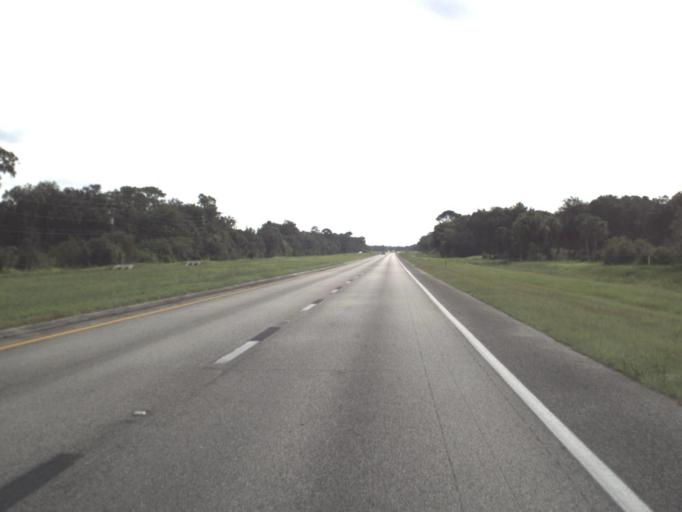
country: US
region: Florida
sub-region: Lee County
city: Alva
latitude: 26.7122
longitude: -81.6498
